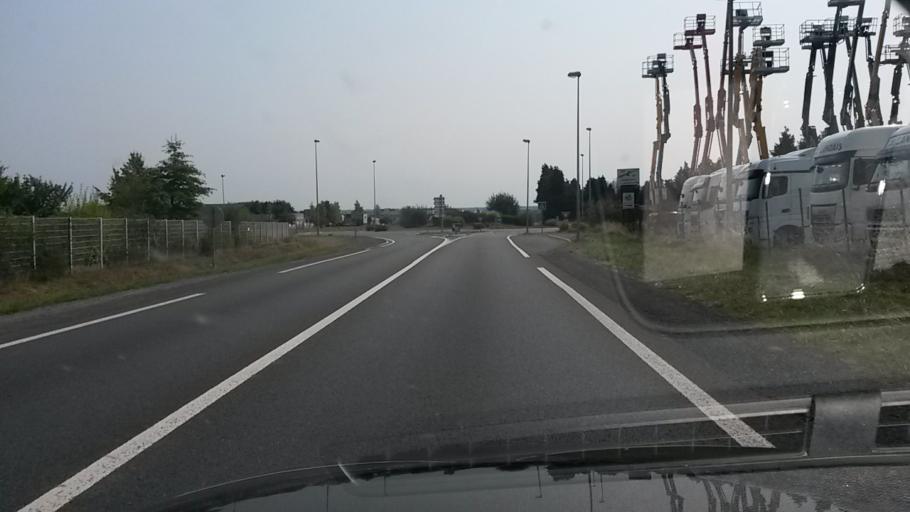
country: FR
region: Pays de la Loire
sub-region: Departement de la Loire-Atlantique
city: Mesanger
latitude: 47.4111
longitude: -1.1898
